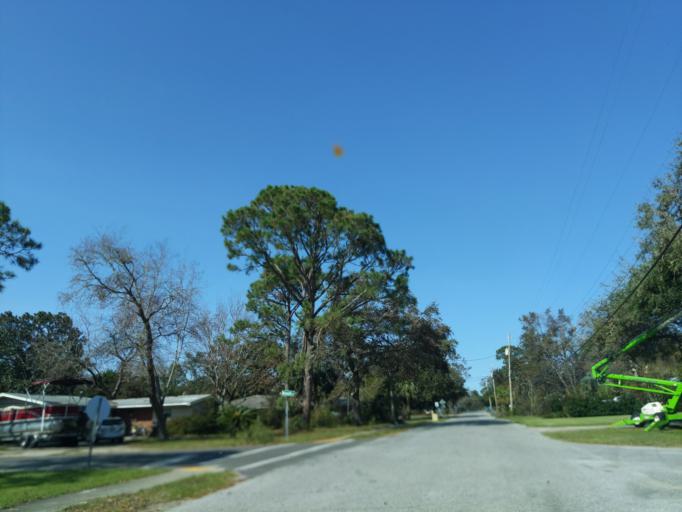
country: US
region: Florida
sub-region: Santa Rosa County
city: Gulf Breeze
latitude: 30.3552
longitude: -87.1872
